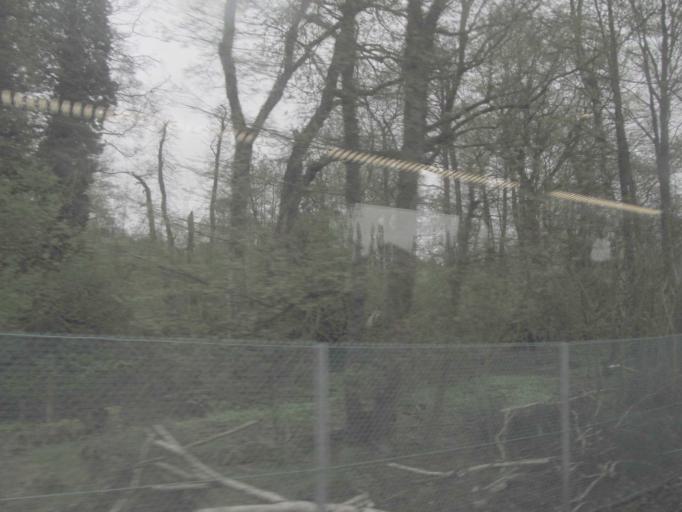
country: GB
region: England
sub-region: Surrey
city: Frimley
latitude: 51.3041
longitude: -0.7437
